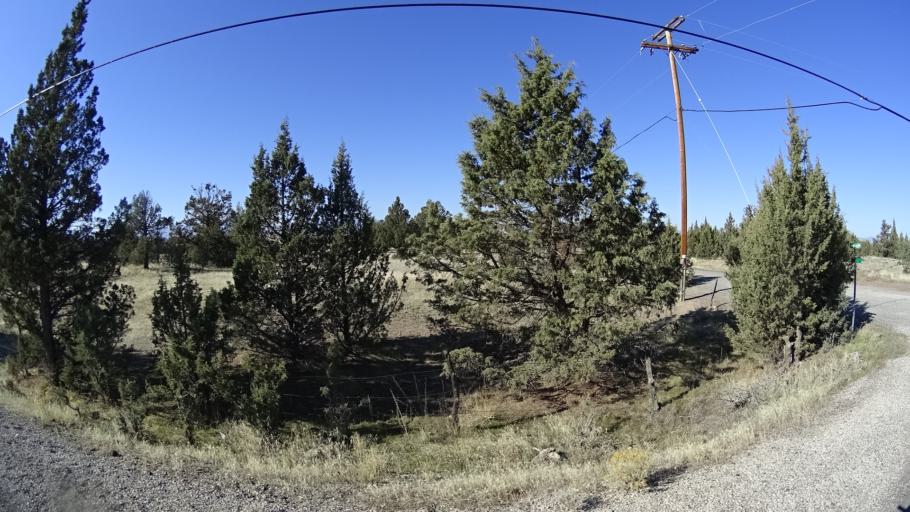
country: US
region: California
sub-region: Siskiyou County
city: Montague
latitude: 41.6492
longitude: -122.3599
